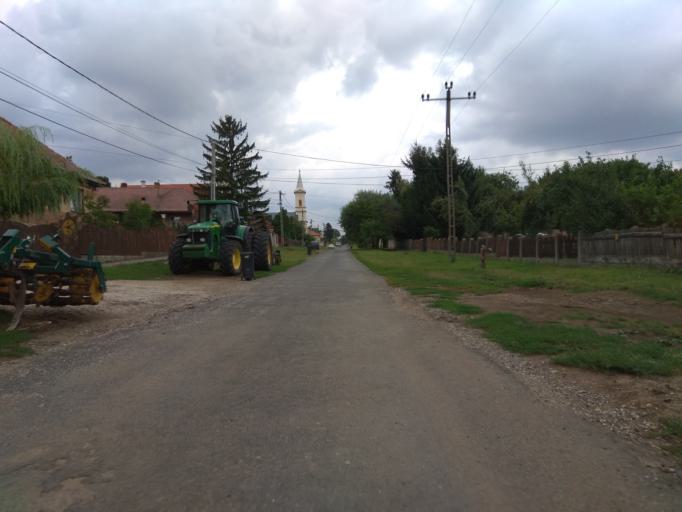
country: HU
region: Borsod-Abauj-Zemplen
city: Gesztely
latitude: 48.1364
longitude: 21.0046
